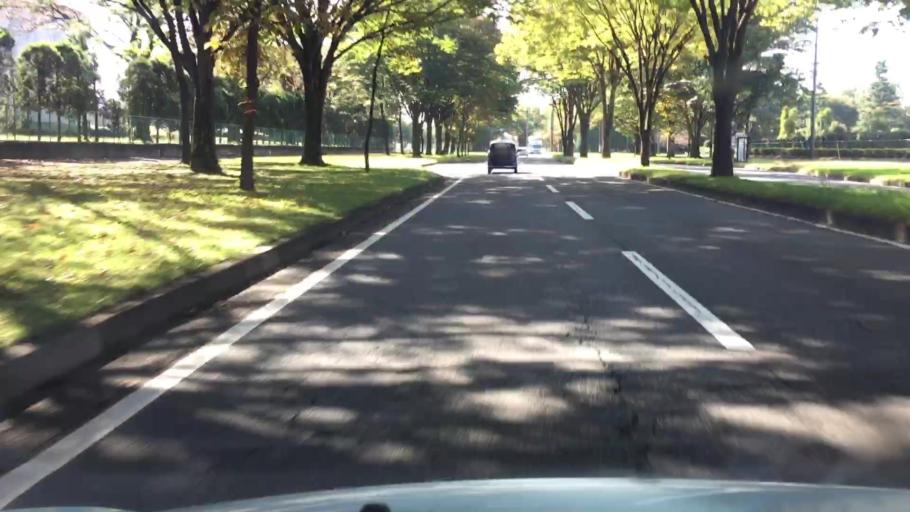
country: JP
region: Tochigi
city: Utsunomiya-shi
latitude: 36.5401
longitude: 139.9873
